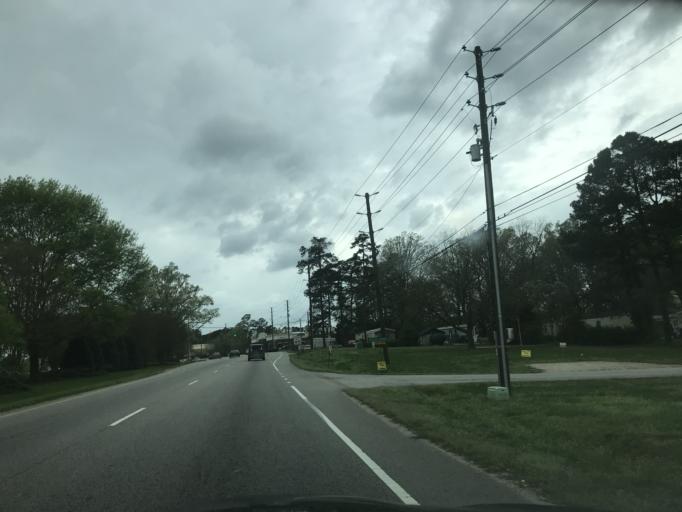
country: US
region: North Carolina
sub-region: Wake County
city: Knightdale
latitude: 35.7988
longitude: -78.4937
